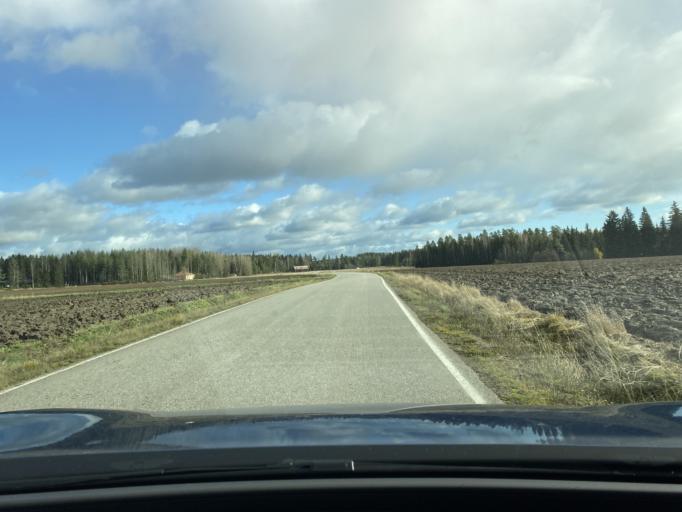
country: FI
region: Varsinais-Suomi
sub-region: Loimaa
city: Aura
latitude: 60.7021
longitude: 22.6155
